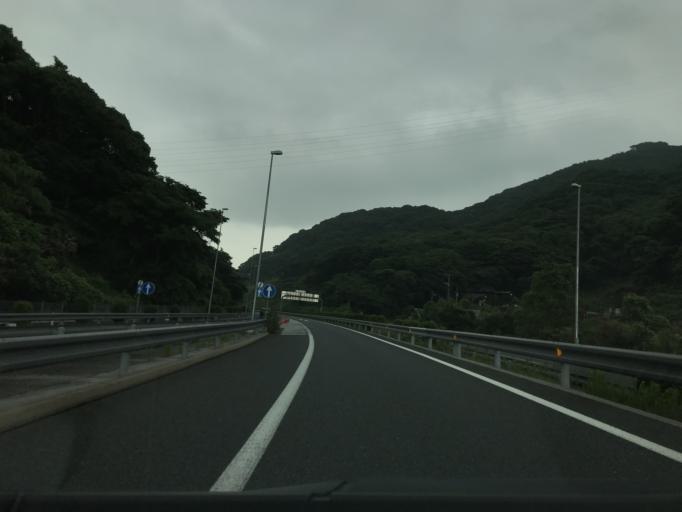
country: JP
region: Fukuoka
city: Kitakyushu
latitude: 33.8147
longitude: 130.8893
